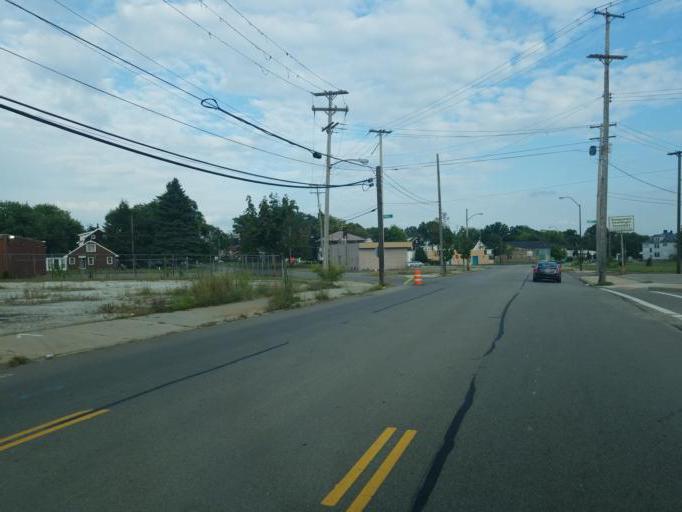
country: US
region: Ohio
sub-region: Mahoning County
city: Youngstown
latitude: 41.1220
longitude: -80.6610
